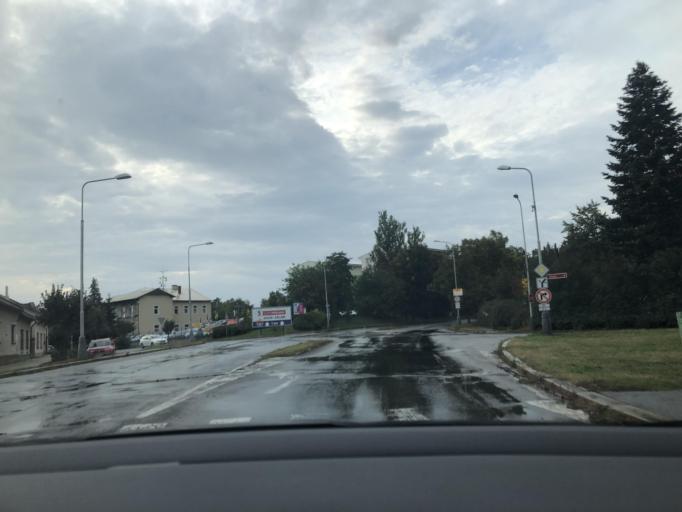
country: CZ
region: Central Bohemia
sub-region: Okres Kolin
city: Kolin
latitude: 50.0331
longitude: 15.2150
